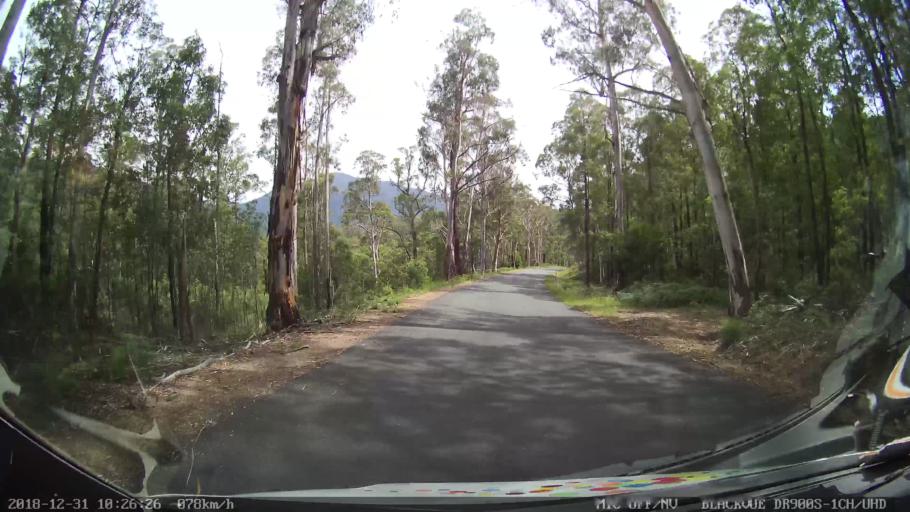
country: AU
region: New South Wales
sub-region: Snowy River
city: Jindabyne
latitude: -36.4957
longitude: 148.1399
